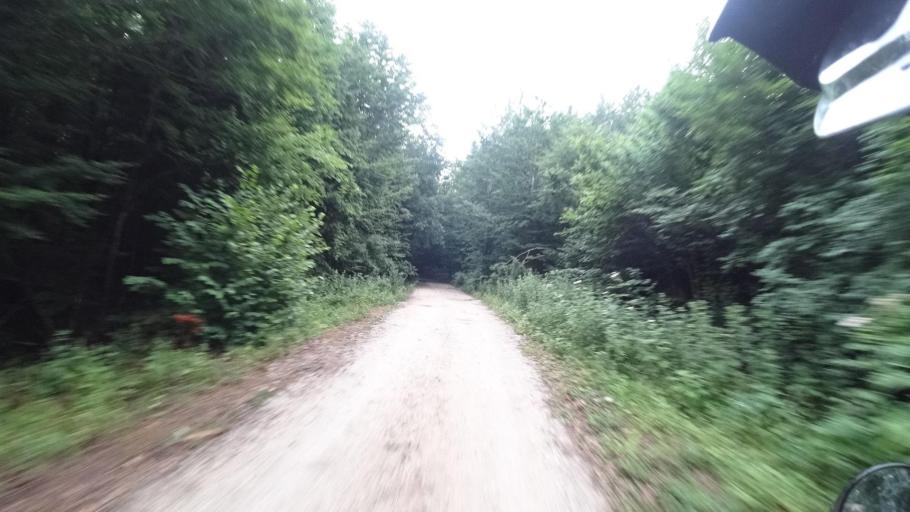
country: BA
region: Federation of Bosnia and Herzegovina
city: Orasac
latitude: 44.5000
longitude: 15.9718
